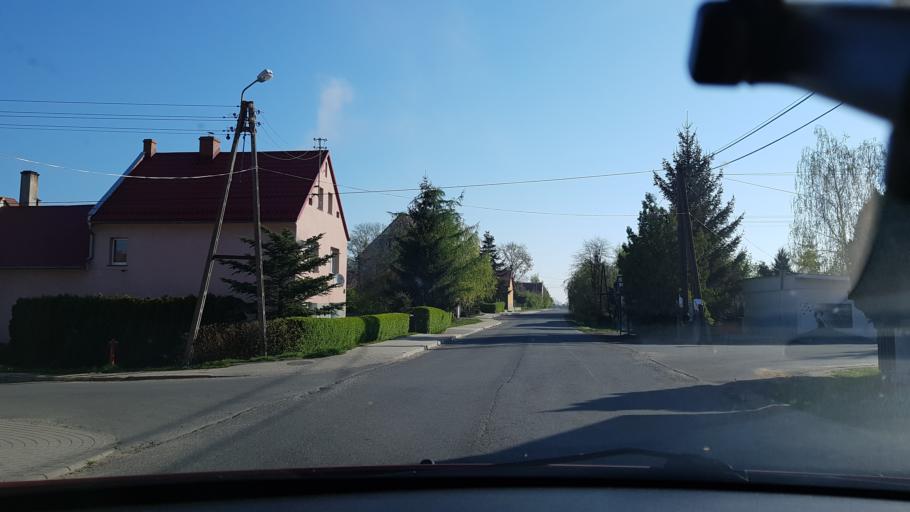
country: CZ
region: Olomoucky
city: Vidnava
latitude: 50.4199
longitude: 17.2252
